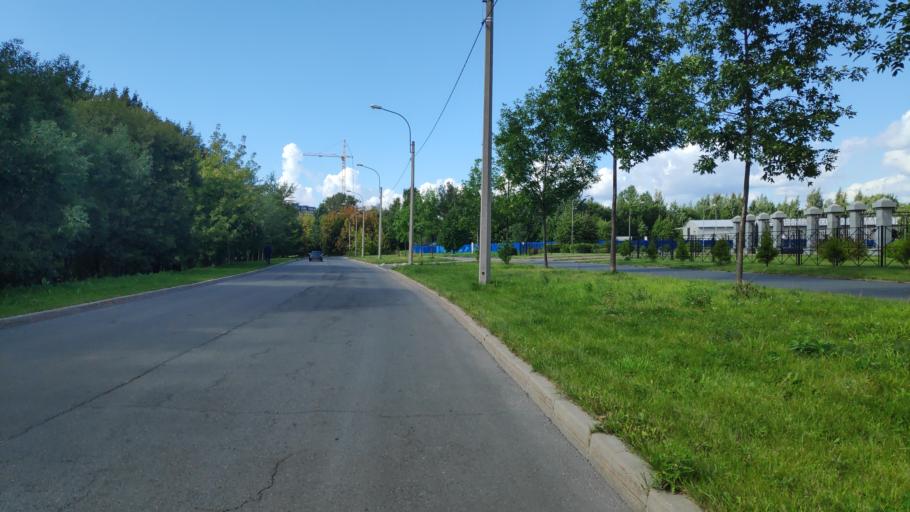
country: RU
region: St.-Petersburg
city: Krasnogvargeisky
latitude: 59.9332
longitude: 30.4273
